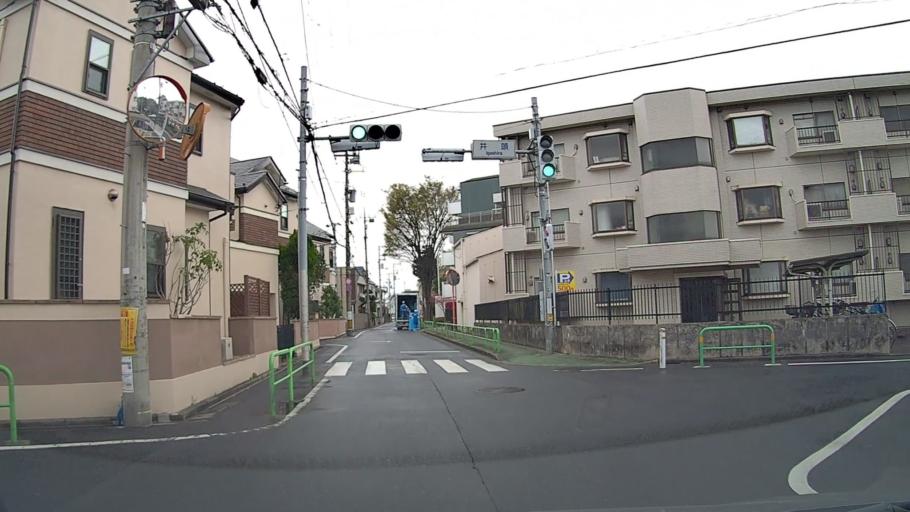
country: JP
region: Tokyo
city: Musashino
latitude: 35.7430
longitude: 139.5806
